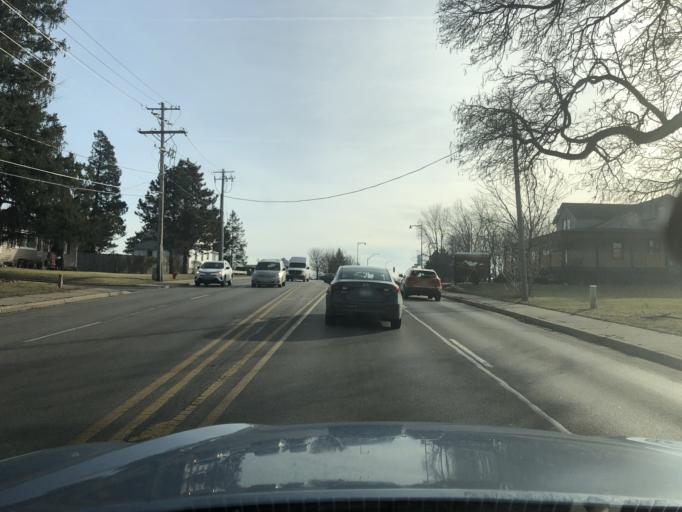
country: US
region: Illinois
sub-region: DuPage County
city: Bloomingdale
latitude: 41.9599
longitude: -88.0815
